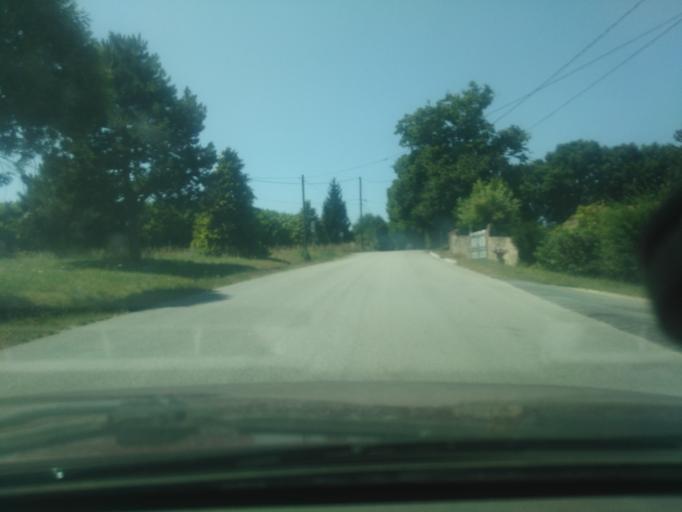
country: FR
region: Pays de la Loire
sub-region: Departement de la Vendee
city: Dompierre-sur-Yon
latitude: 46.7159
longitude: -1.4013
